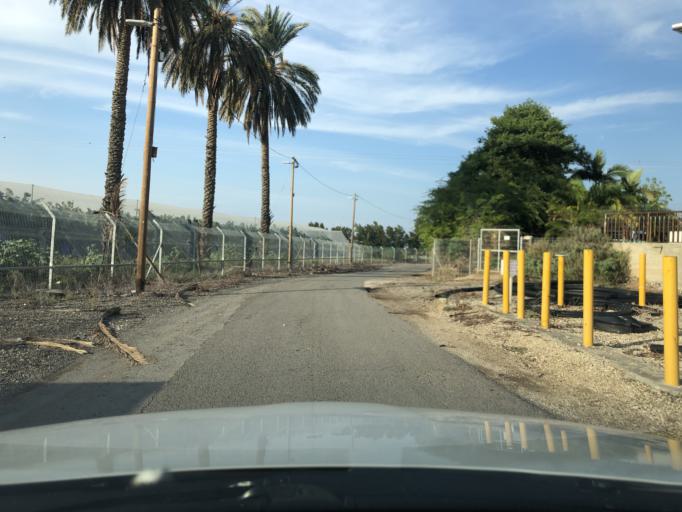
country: IL
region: Northern District
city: Yavne'el
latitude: 32.6627
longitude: 35.5800
